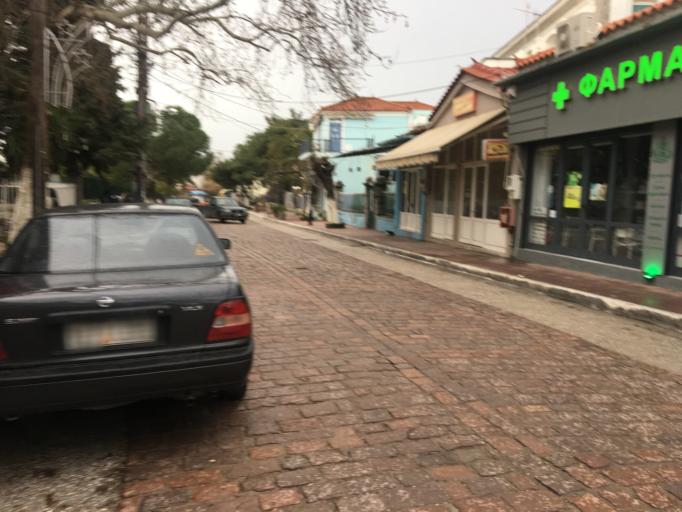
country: GR
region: North Aegean
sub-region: Nomos Lesvou
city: Agia Paraskevi
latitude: 39.2470
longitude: 26.2715
